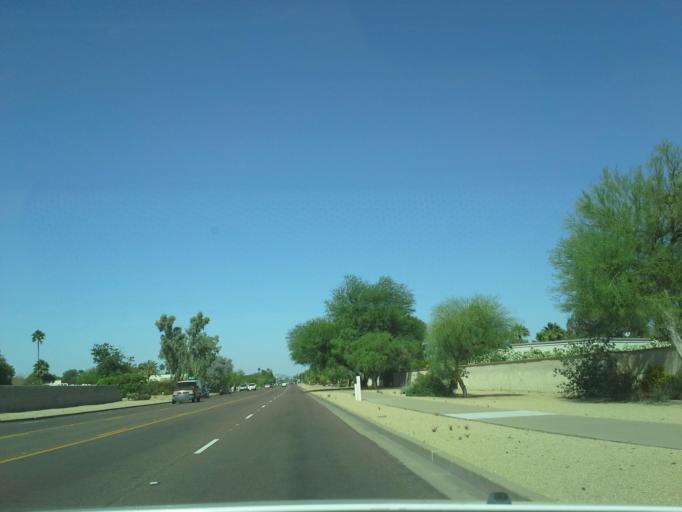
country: US
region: Arizona
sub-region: Maricopa County
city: Paradise Valley
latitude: 33.5967
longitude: -111.9167
